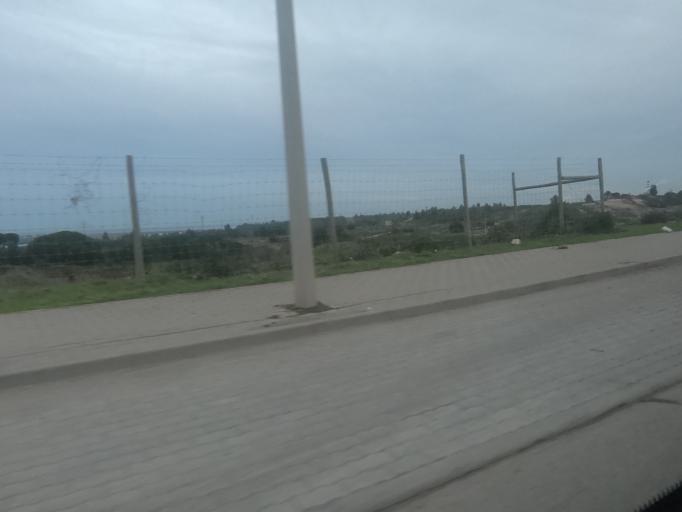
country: PT
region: Setubal
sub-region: Setubal
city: Setubal
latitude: 38.5062
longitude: -8.8310
